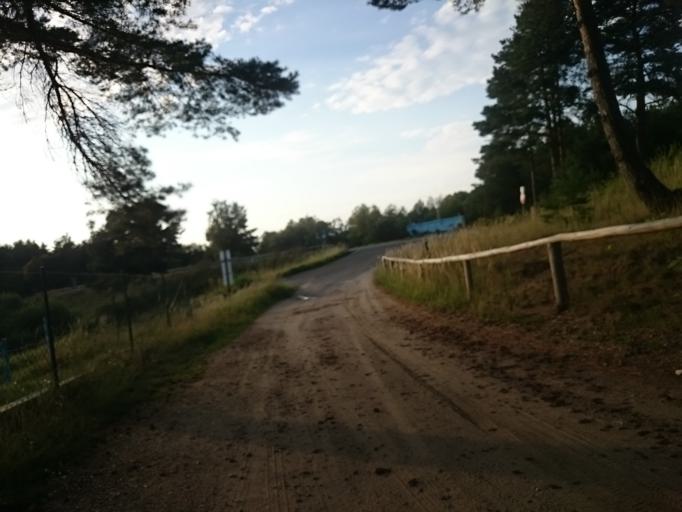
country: DE
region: Mecklenburg-Vorpommern
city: Neustrelitz
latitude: 53.3000
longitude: 13.0802
